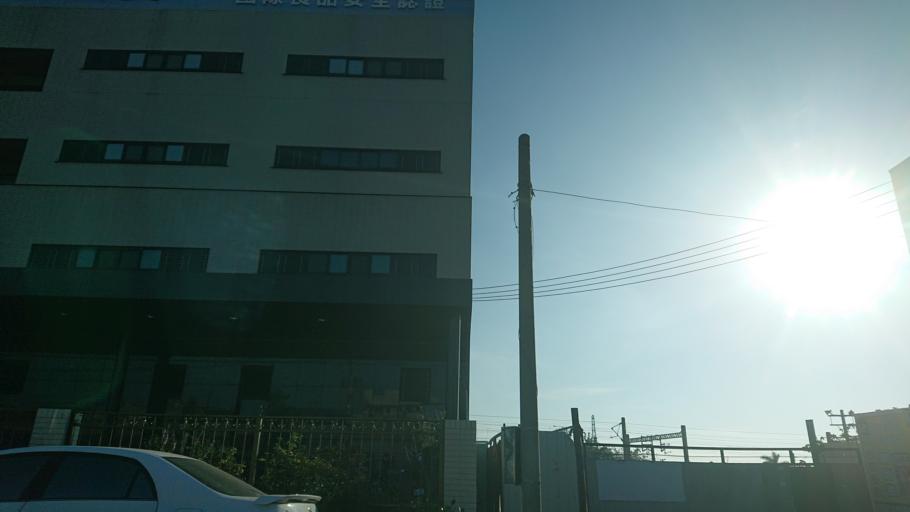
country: TW
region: Taiwan
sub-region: Changhua
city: Chang-hua
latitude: 24.1206
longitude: 120.5714
